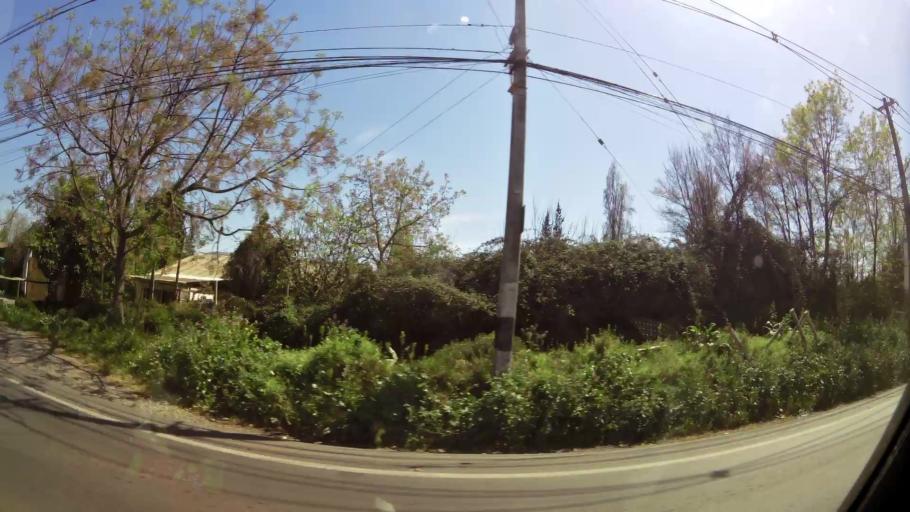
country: CL
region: Santiago Metropolitan
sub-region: Provincia de Talagante
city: Talagante
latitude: -33.6303
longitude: -70.9105
